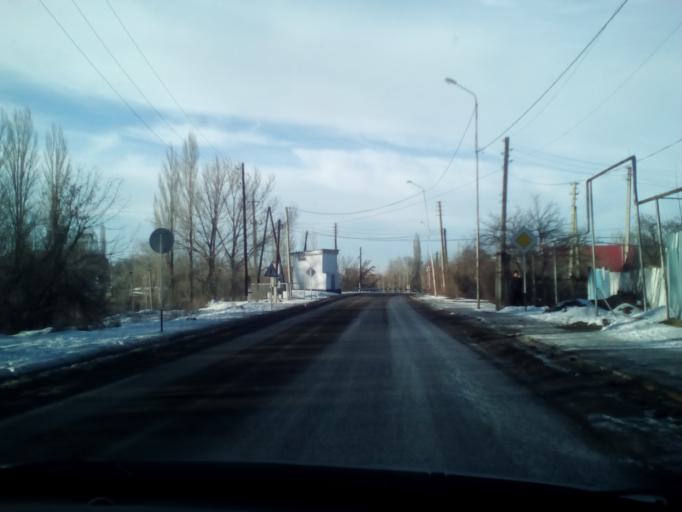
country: KZ
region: Almaty Oblysy
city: Burunday
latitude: 43.1592
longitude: 76.4180
